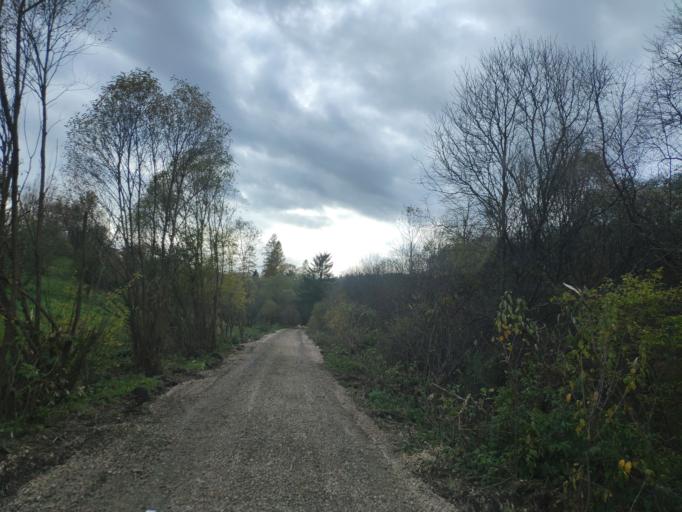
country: SK
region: Kosicky
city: Spisska Nova Ves
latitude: 48.8313
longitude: 20.6334
